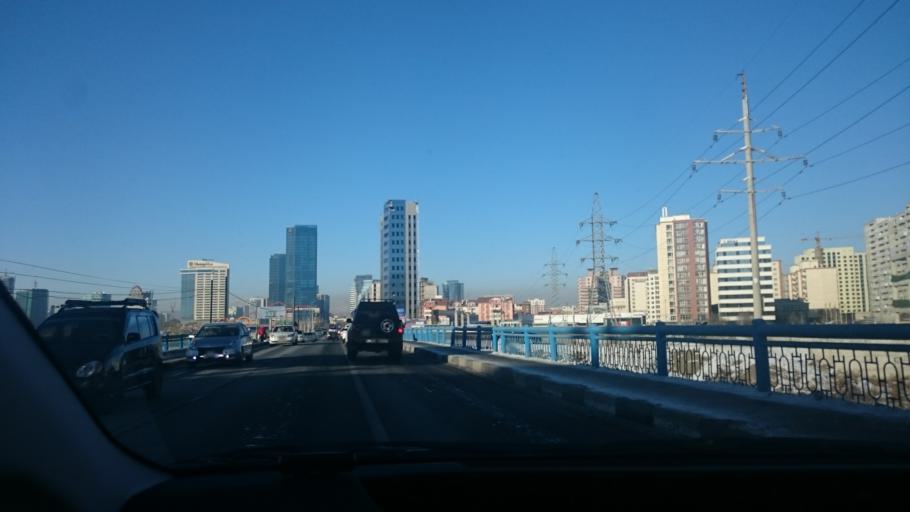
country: MN
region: Ulaanbaatar
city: Ulaanbaatar
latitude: 47.9062
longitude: 106.9275
